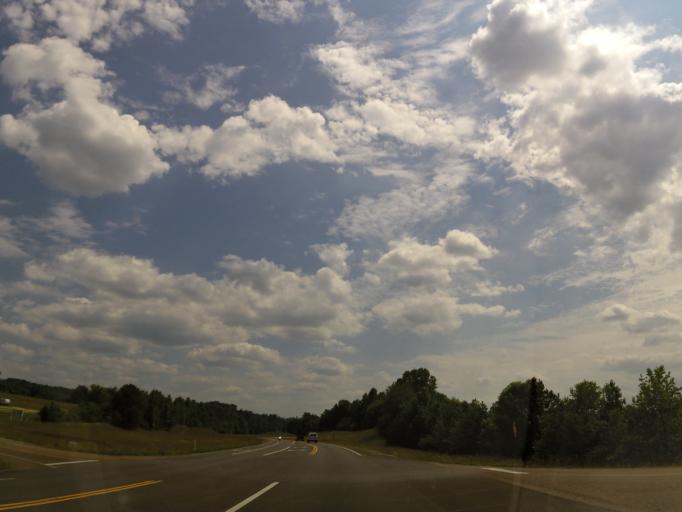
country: US
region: Tennessee
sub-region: Marion County
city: Whitwell
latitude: 35.1514
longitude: -85.5427
